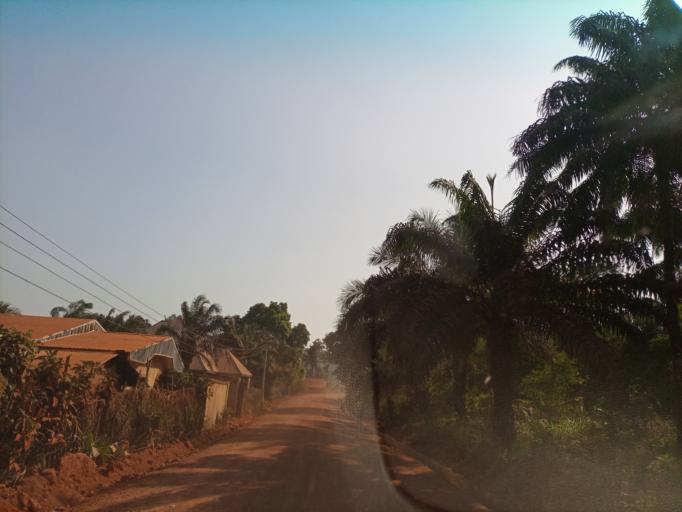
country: NG
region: Enugu
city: Aku
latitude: 6.7030
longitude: 7.3211
